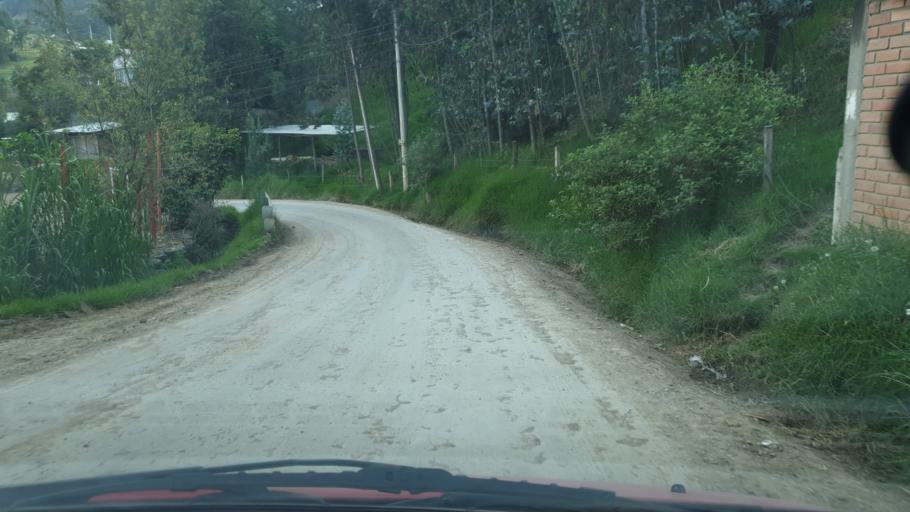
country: EC
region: Azuay
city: Cuenca
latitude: -2.9194
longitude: -78.9790
